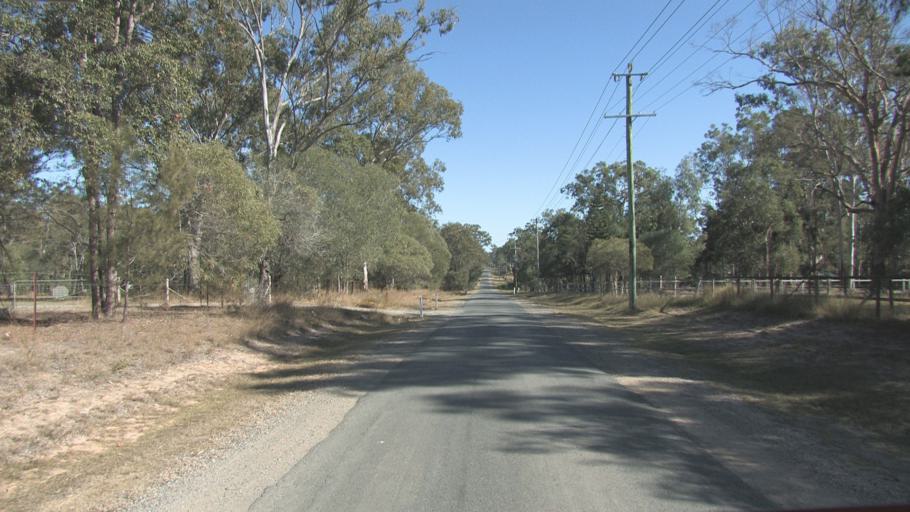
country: AU
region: Queensland
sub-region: Logan
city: North Maclean
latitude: -27.7994
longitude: 153.0518
